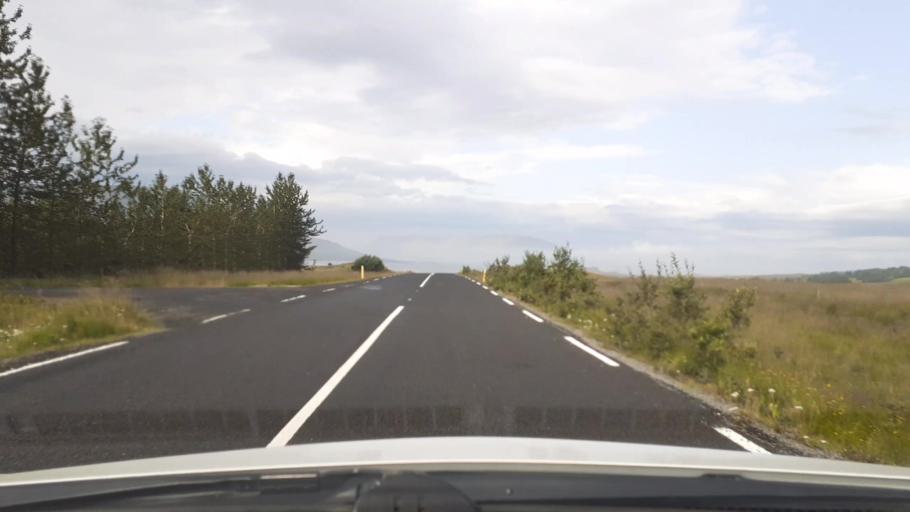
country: IS
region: Capital Region
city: Mosfellsbaer
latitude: 64.3424
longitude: -21.5925
